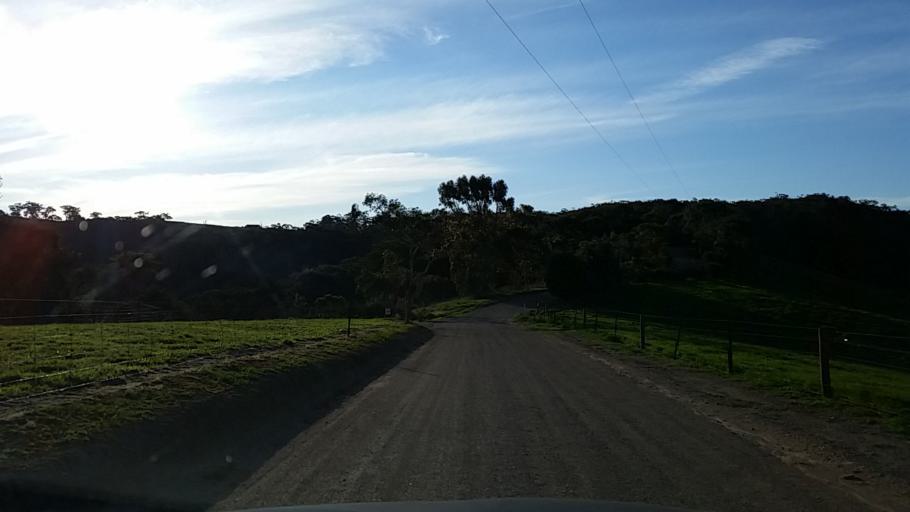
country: AU
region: South Australia
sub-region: Mount Barker
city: Meadows
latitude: -35.2399
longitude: 138.7556
